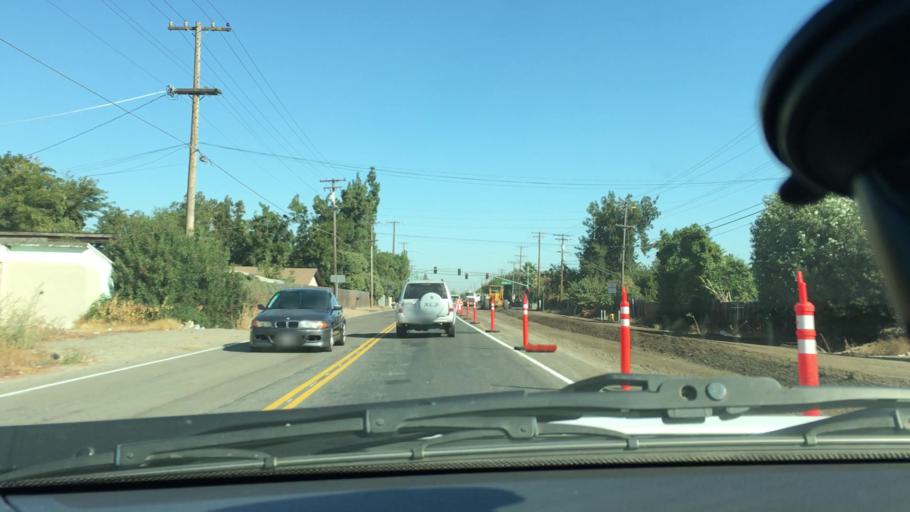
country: US
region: California
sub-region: Stanislaus County
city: West Modesto
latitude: 37.6199
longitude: -121.0304
